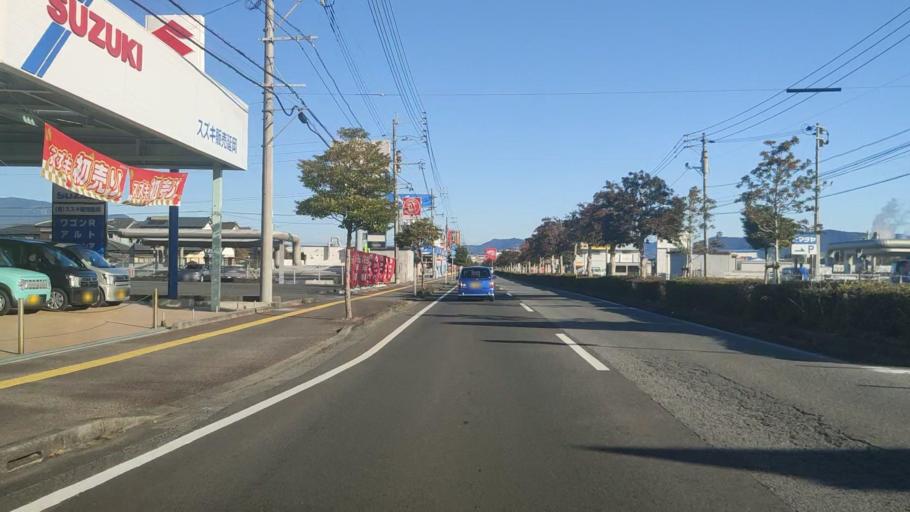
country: JP
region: Miyazaki
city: Nobeoka
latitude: 32.5638
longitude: 131.6818
